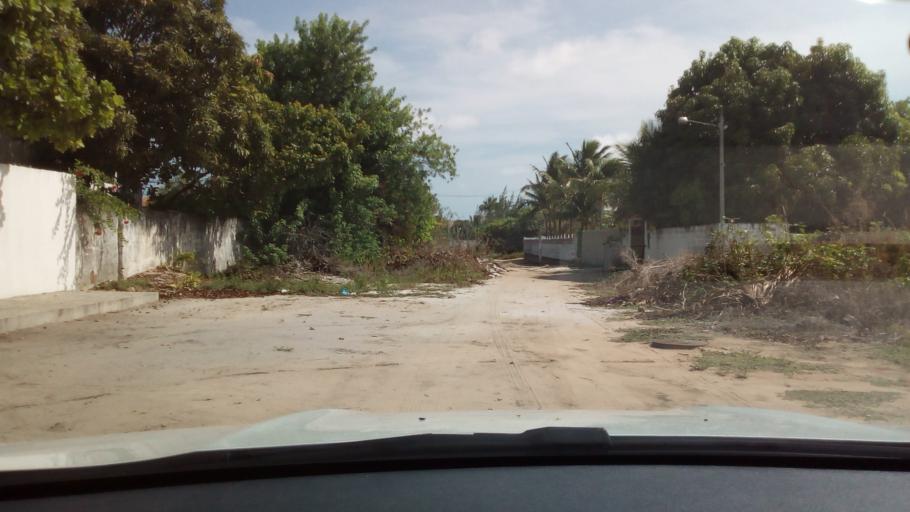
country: BR
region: Paraiba
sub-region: Conde
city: Conde
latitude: -7.2964
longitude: -34.8028
